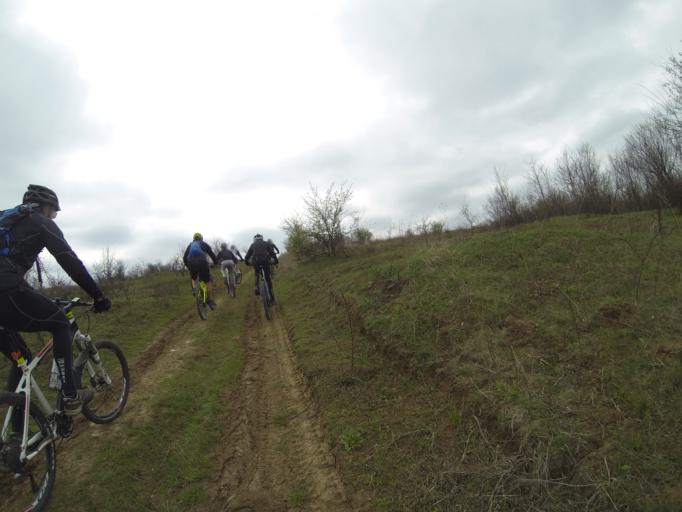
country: RO
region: Dolj
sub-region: Comuna Predesti
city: Predesti
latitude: 44.3279
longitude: 23.6222
